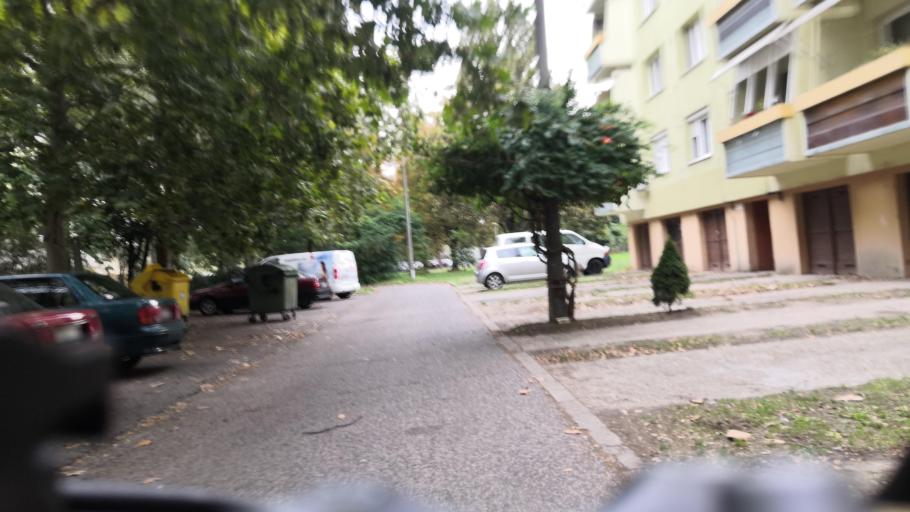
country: HU
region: Csongrad
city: Szeged
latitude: 46.2747
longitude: 20.1615
